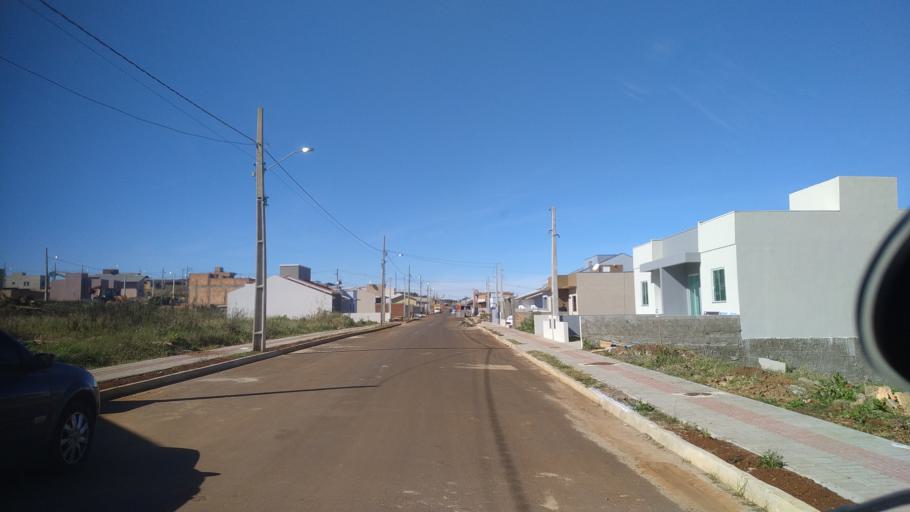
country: BR
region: Santa Catarina
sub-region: Chapeco
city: Chapeco
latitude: -27.0500
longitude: -52.5983
